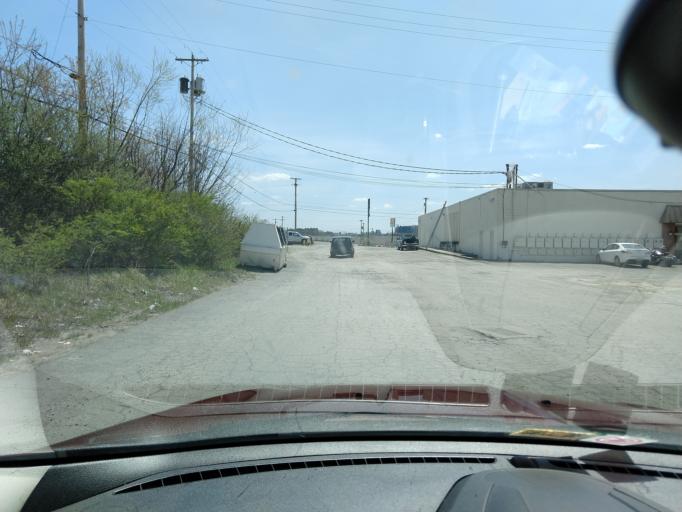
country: US
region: West Virginia
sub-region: Raleigh County
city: Prosperity
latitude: 37.8119
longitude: -81.1834
